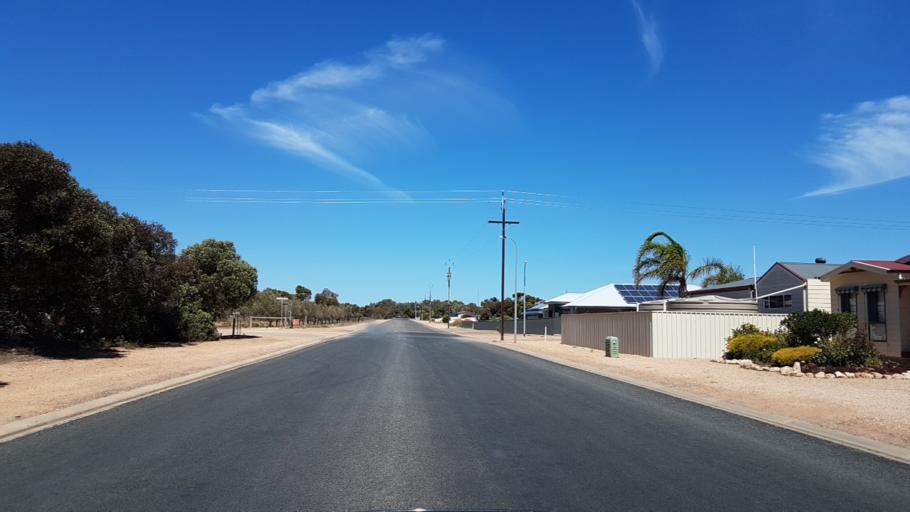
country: AU
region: South Australia
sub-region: Copper Coast
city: Wallaroo
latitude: -34.0559
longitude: 137.5807
